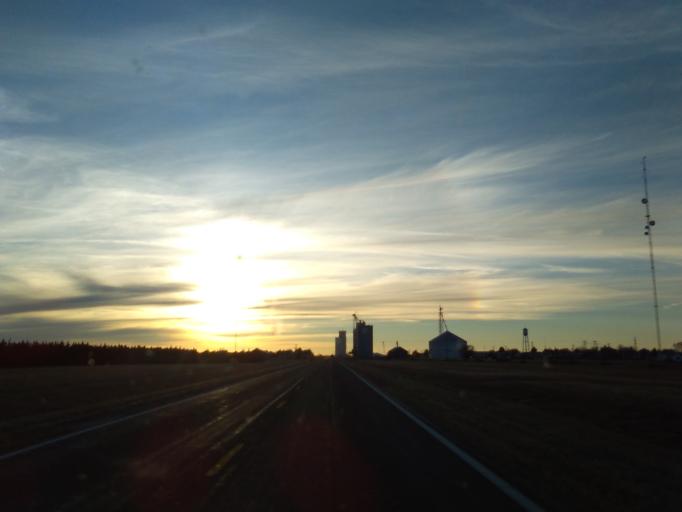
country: US
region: Kansas
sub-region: Logan County
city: Oakley
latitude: 39.0620
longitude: -101.2345
